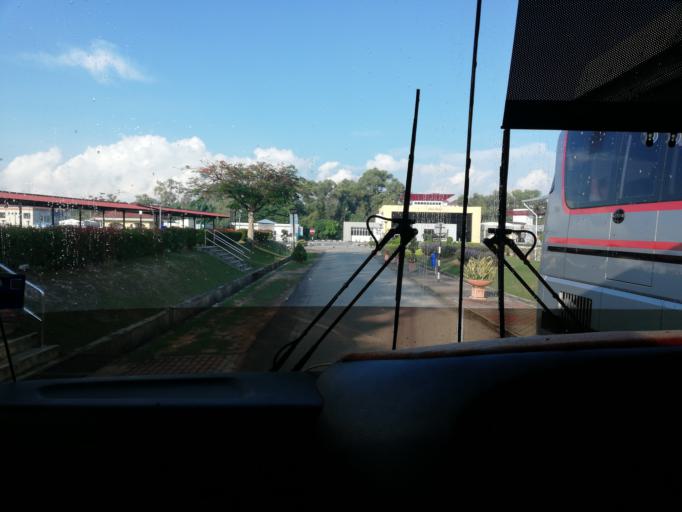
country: MY
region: Negeri Sembilan
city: Port Dickson
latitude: 2.4424
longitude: 101.8629
